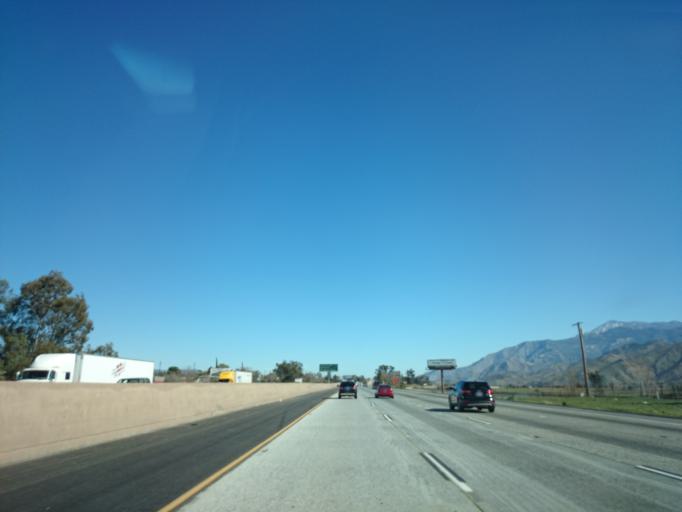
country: US
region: California
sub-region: Riverside County
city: Banning
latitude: 33.9260
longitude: -116.9248
